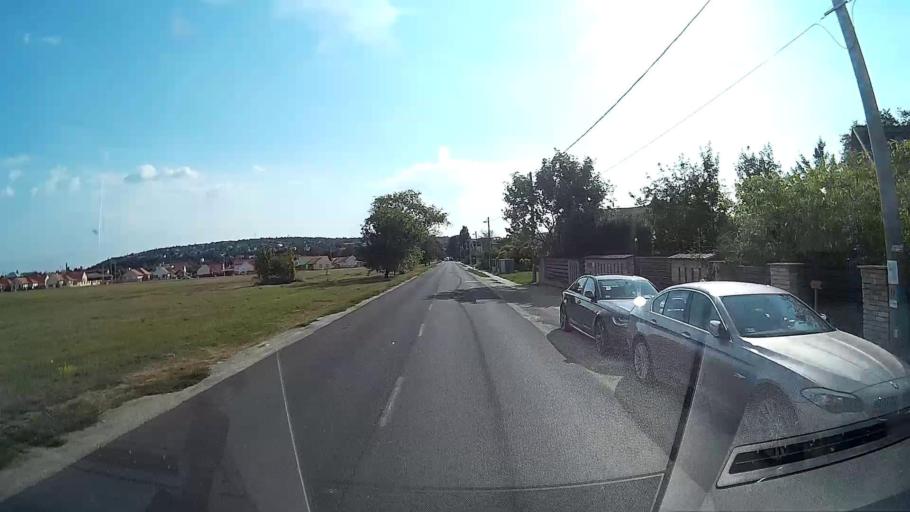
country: HU
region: Pest
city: Budakalasz
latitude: 47.6266
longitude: 19.0548
